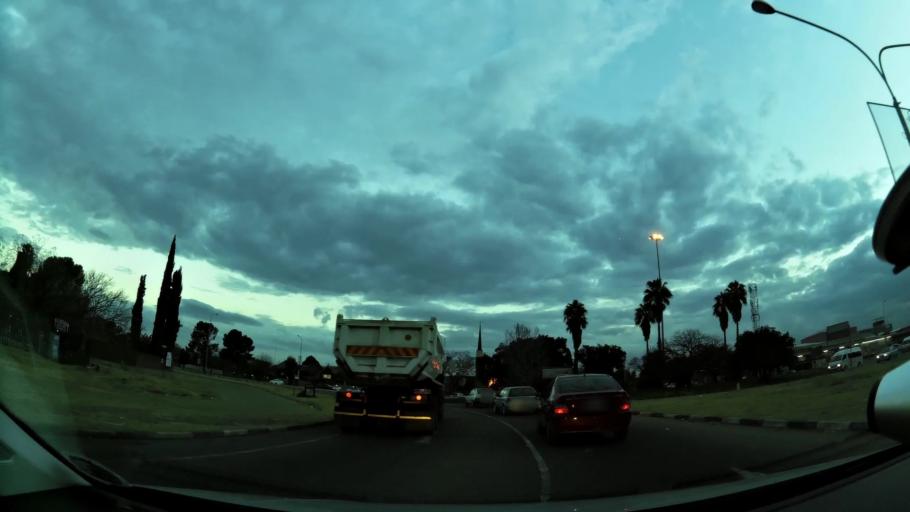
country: ZA
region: Orange Free State
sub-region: Lejweleputswa District Municipality
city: Welkom
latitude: -27.9814
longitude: 26.7425
